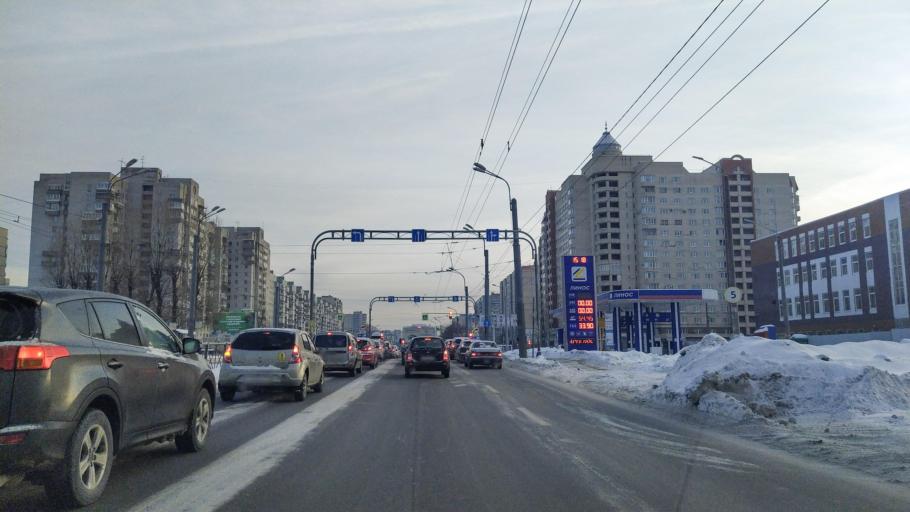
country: RU
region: St.-Petersburg
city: Krasnogvargeisky
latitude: 59.9570
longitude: 30.4656
